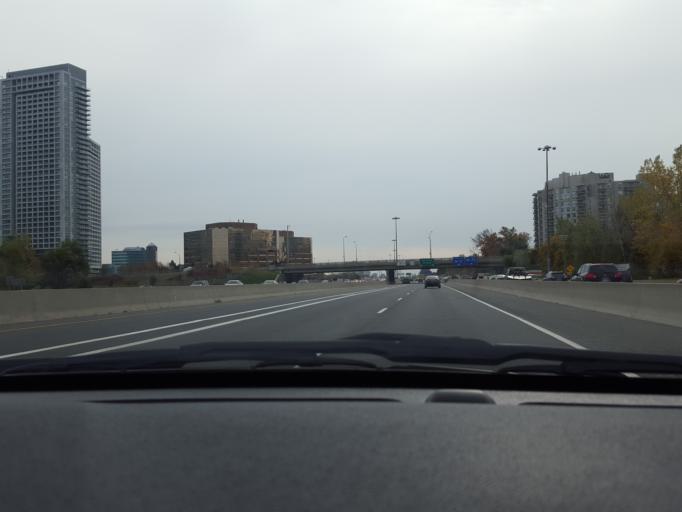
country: CA
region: Ontario
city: Willowdale
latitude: 43.7781
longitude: -79.3403
